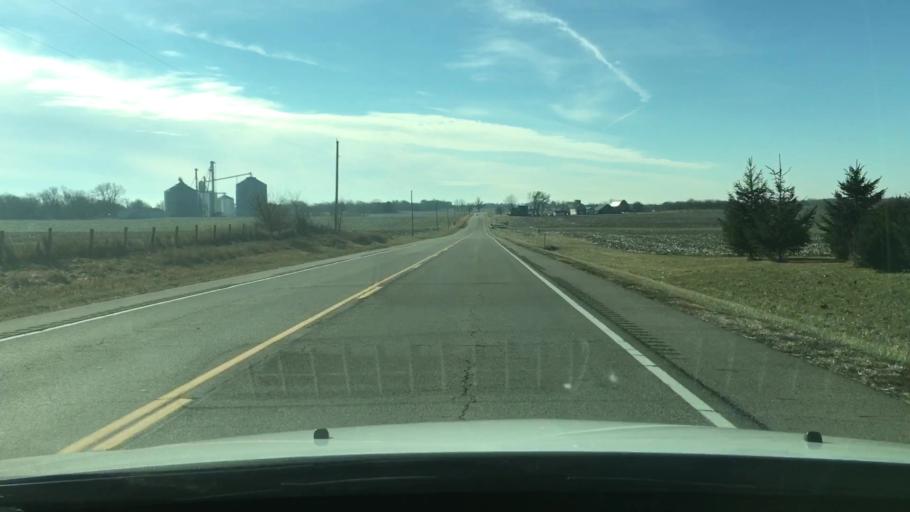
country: US
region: Illinois
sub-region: Woodford County
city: Washburn
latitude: 40.8829
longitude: -89.3155
